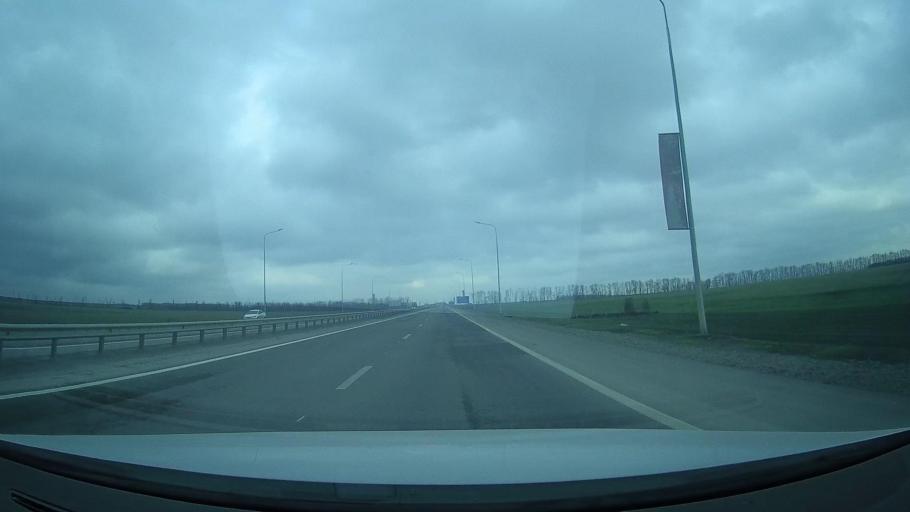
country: RU
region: Rostov
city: Grushevskaya
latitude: 47.4961
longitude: 39.9565
